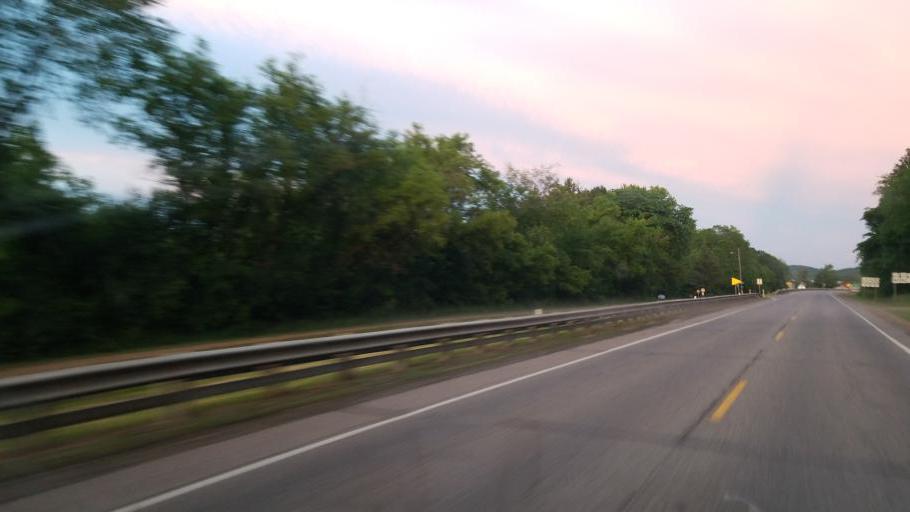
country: US
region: Wisconsin
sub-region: Juneau County
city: Elroy
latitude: 43.7453
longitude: -90.2772
